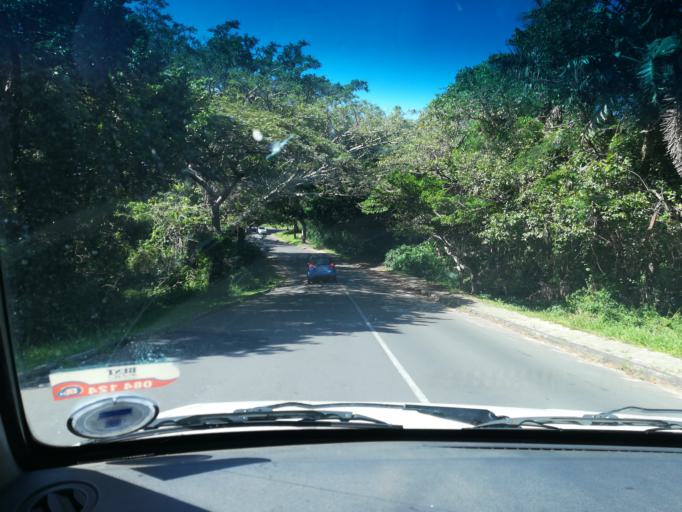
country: ZA
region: KwaZulu-Natal
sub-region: Ugu District Municipality
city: Scottburgh
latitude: -30.3799
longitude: 30.6897
